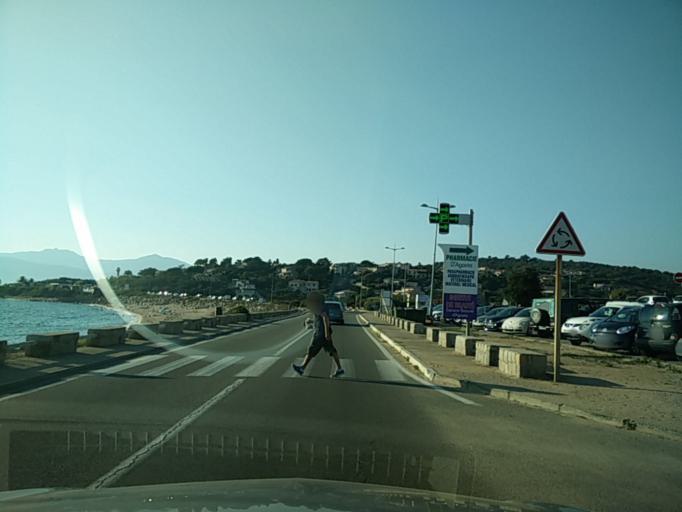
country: FR
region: Corsica
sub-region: Departement de la Corse-du-Sud
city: Pietrosella
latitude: 41.8664
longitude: 8.7911
